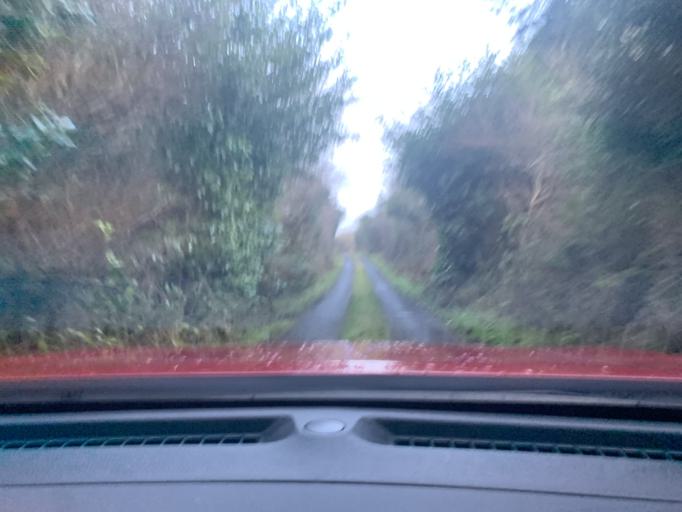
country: IE
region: Connaught
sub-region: Sligo
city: Ballymote
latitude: 53.9887
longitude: -8.4423
